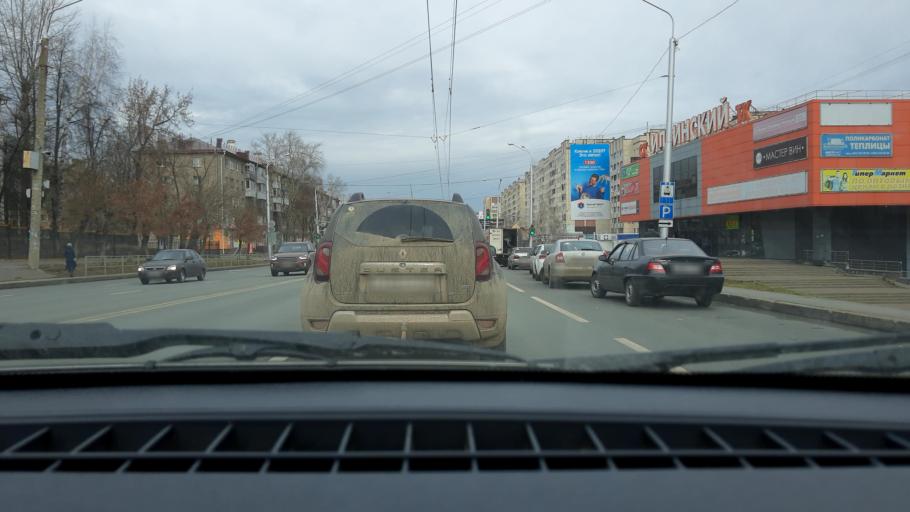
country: RU
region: Bashkortostan
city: Ufa
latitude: 54.7757
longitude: 56.0348
